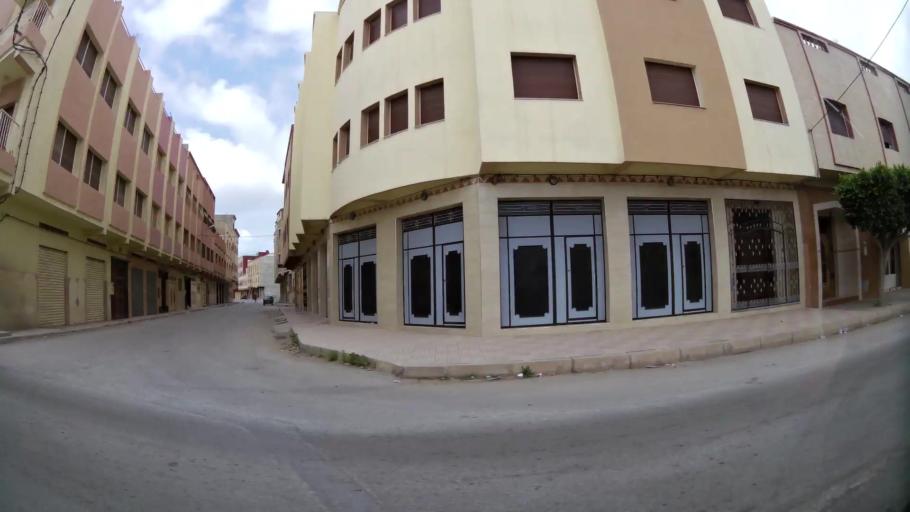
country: MA
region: Oriental
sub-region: Nador
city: Nador
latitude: 35.1612
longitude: -2.9397
